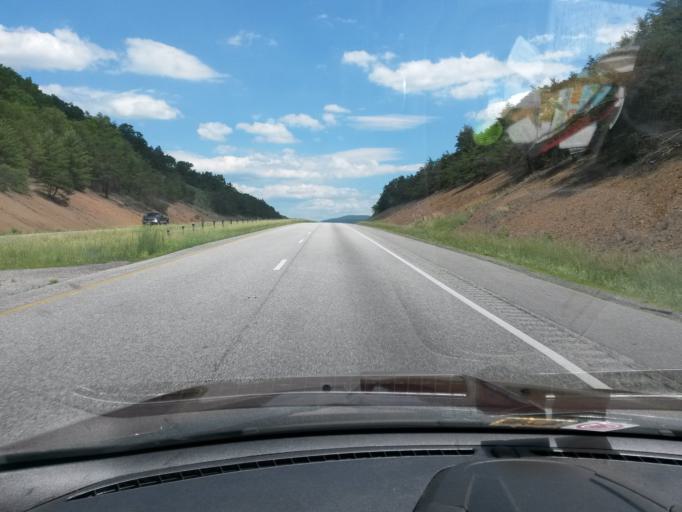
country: US
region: Virginia
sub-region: City of Covington
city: Covington
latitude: 37.7938
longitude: -80.0437
